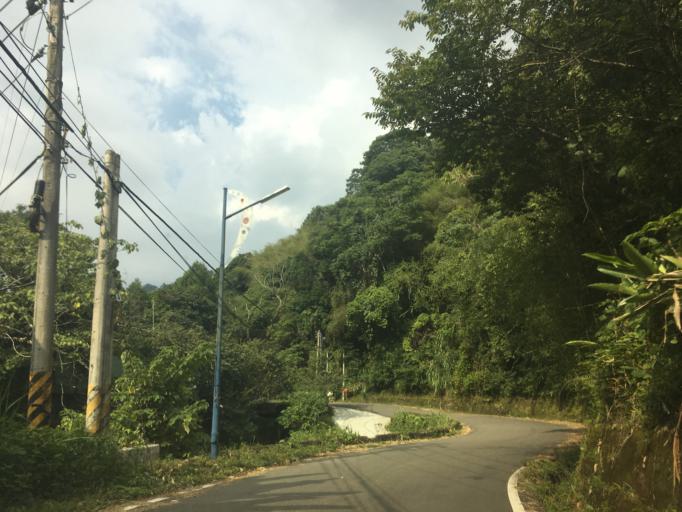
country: TW
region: Taiwan
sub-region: Miaoli
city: Miaoli
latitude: 24.3702
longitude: 120.9663
